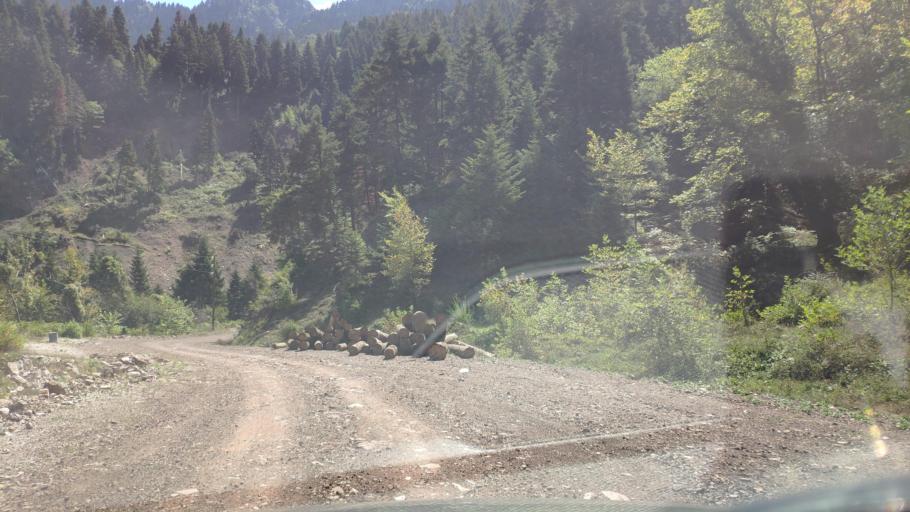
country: GR
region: Central Greece
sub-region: Nomos Evrytanias
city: Kerasochori
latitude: 39.1140
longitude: 21.6212
